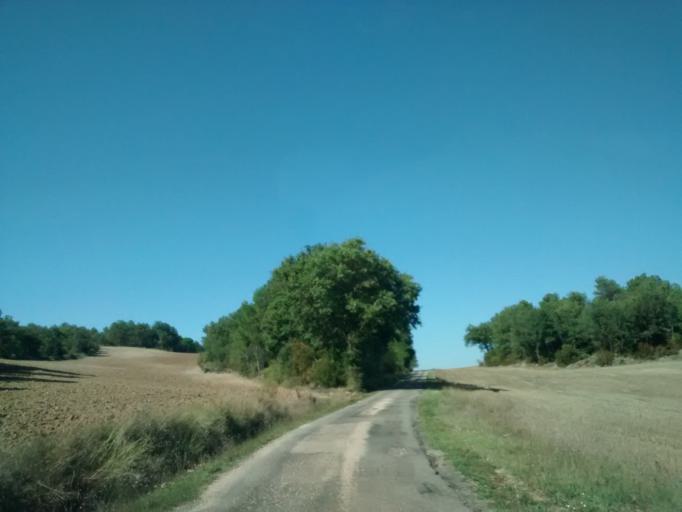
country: ES
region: Aragon
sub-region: Provincia de Huesca
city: Santa Cruz de la Seros
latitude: 42.4331
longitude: -0.6343
